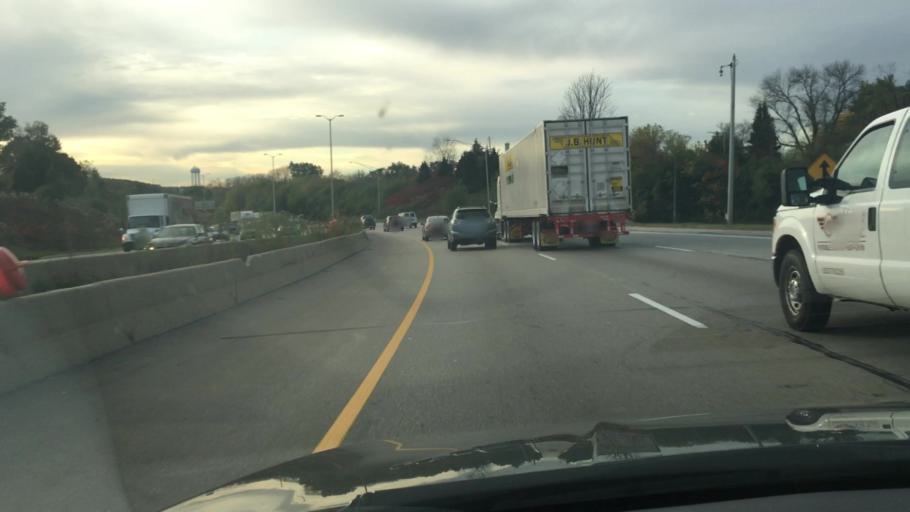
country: US
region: Wisconsin
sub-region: Waukesha County
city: Elm Grove
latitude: 43.0593
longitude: -88.0533
